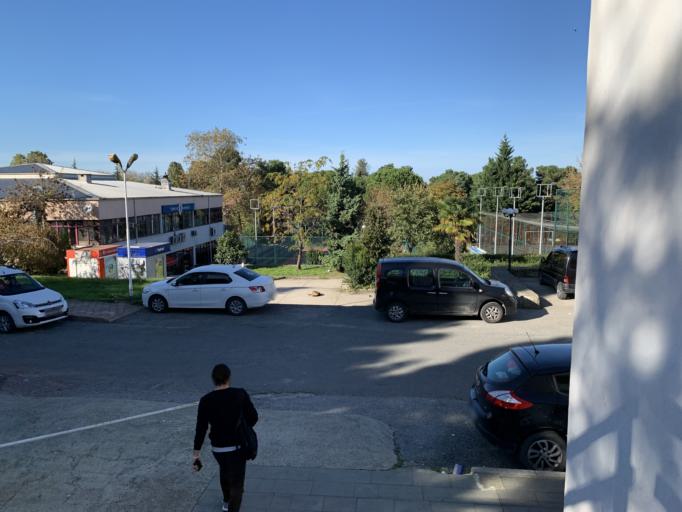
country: TR
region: Trabzon
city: Trabzon
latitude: 40.9961
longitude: 39.7687
